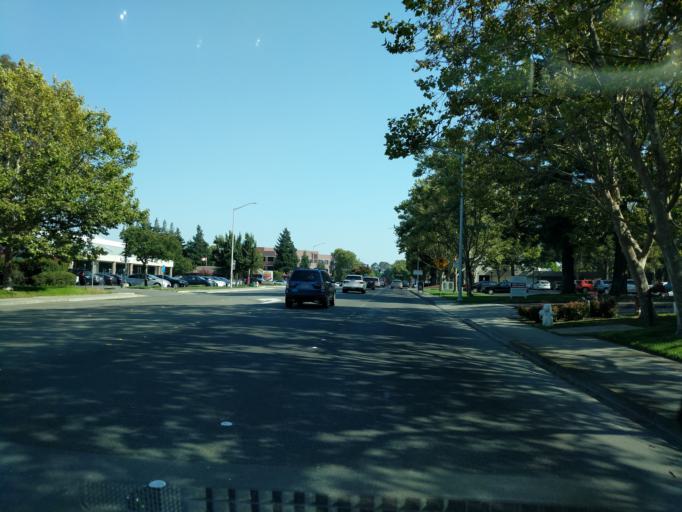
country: US
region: California
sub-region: Contra Costa County
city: San Ramon
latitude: 37.7811
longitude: -121.9701
